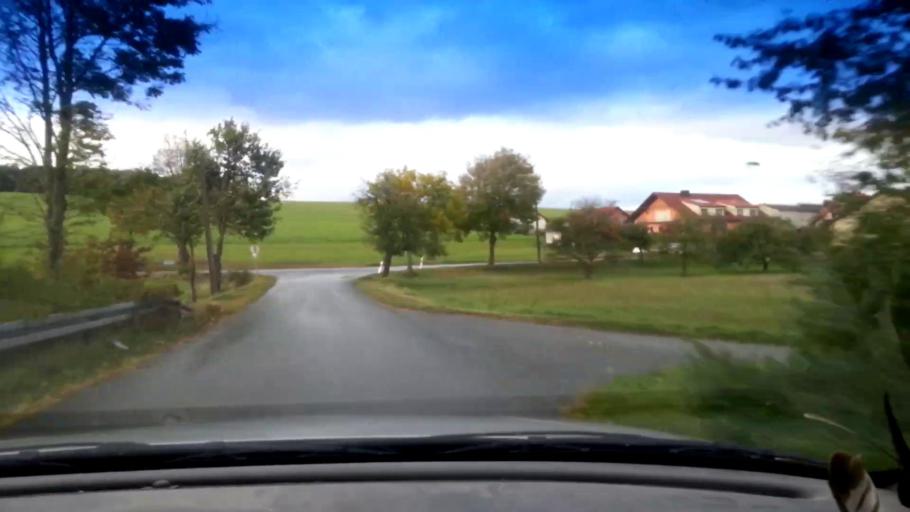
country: DE
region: Bavaria
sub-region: Upper Franconia
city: Burgwindheim
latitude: 49.8084
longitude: 10.6388
